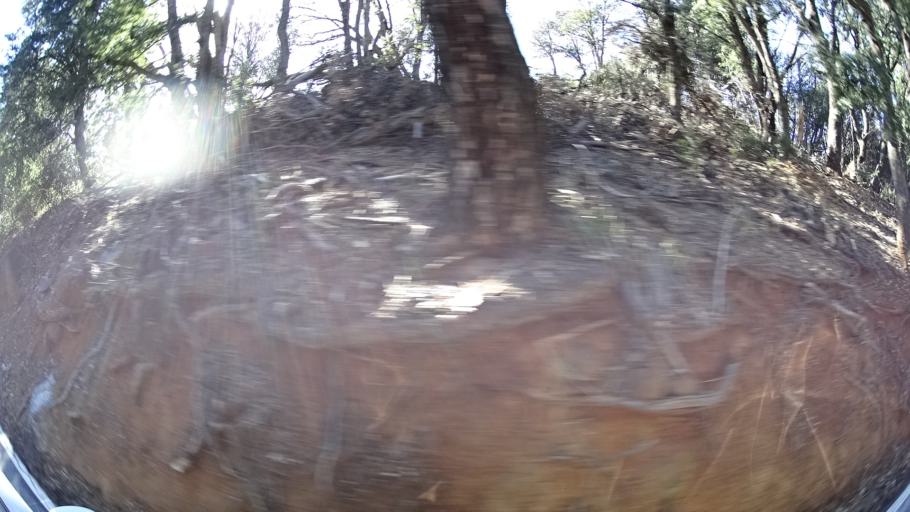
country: US
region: California
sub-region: San Diego County
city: Julian
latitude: 33.0318
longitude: -116.5615
